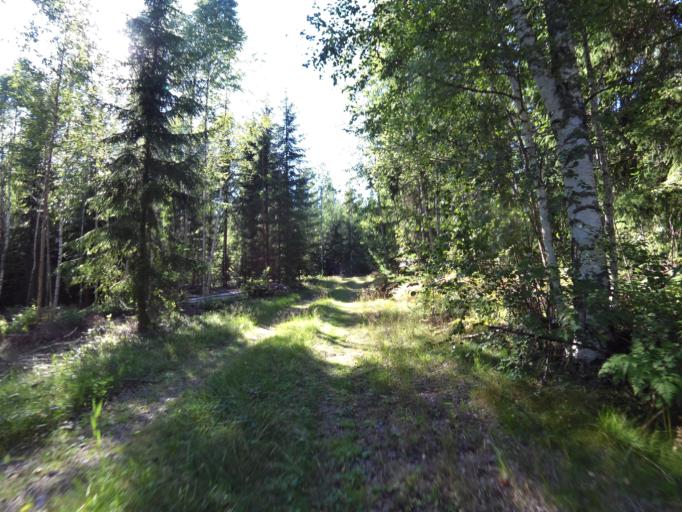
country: SE
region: Gaevleborg
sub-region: Hofors Kommun
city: Hofors
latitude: 60.5706
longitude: 16.4534
